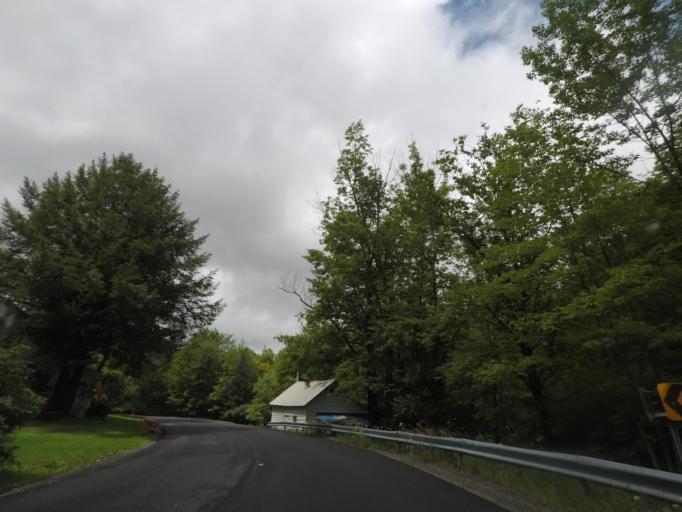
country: US
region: New York
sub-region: Rensselaer County
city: Poestenkill
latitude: 42.6894
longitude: -73.4751
